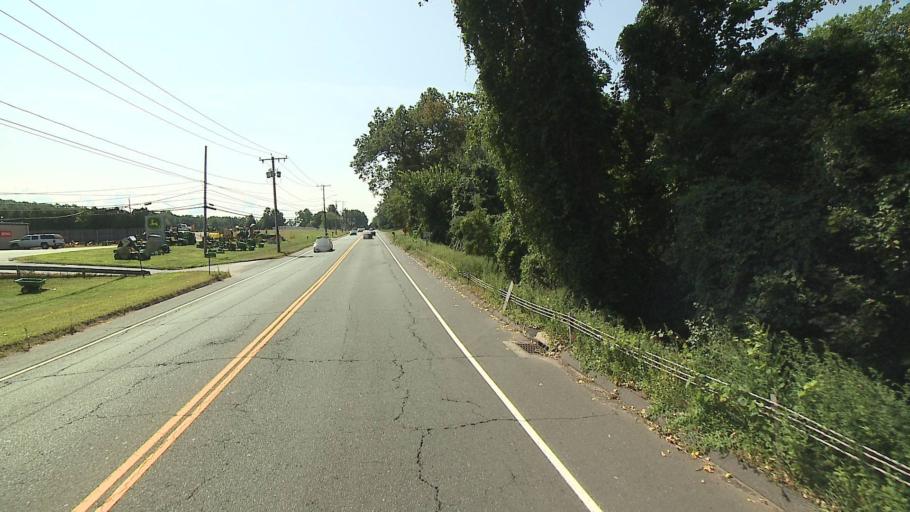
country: US
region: Connecticut
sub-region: Hartford County
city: Windsor Locks
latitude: 41.8980
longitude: -72.6082
